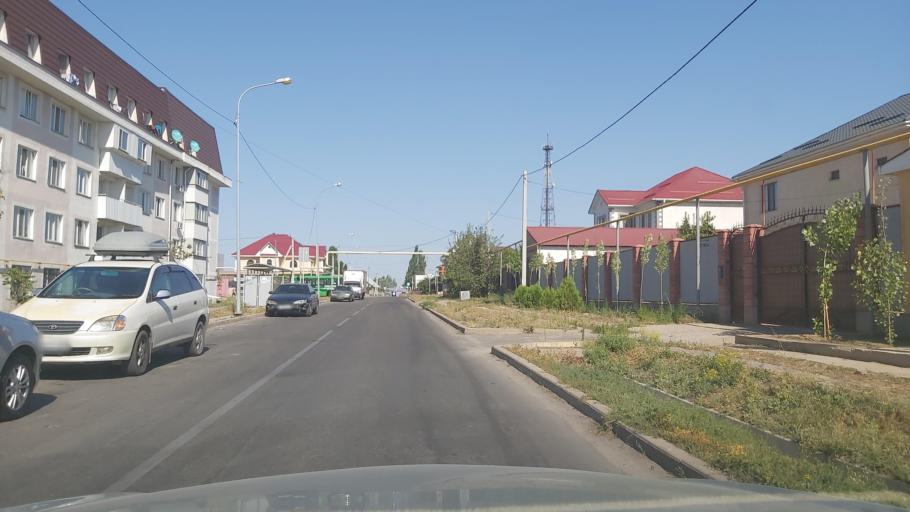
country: KZ
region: Almaty Oblysy
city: Burunday
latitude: 43.3185
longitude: 76.8403
